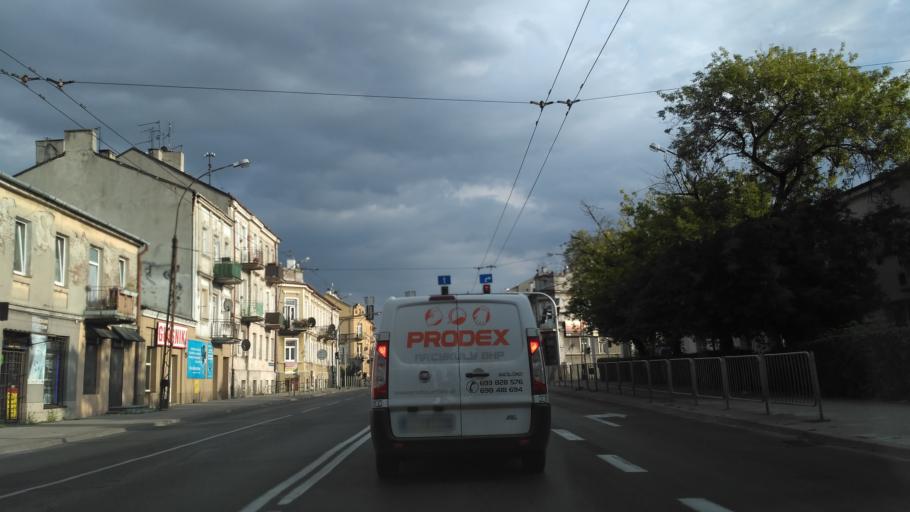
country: PL
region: Lublin Voivodeship
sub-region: Powiat lubelski
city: Lublin
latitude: 51.2292
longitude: 22.5722
